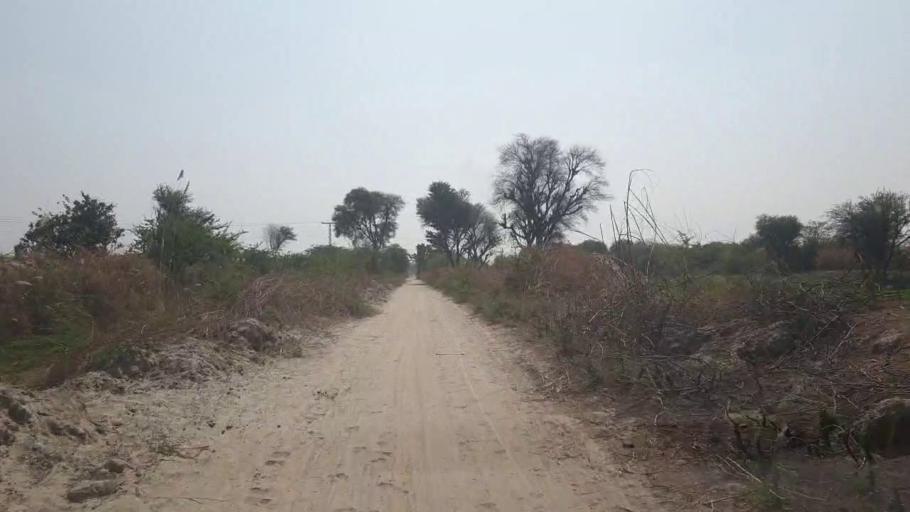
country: PK
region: Sindh
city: Dhoro Naro
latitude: 25.5105
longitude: 69.5424
